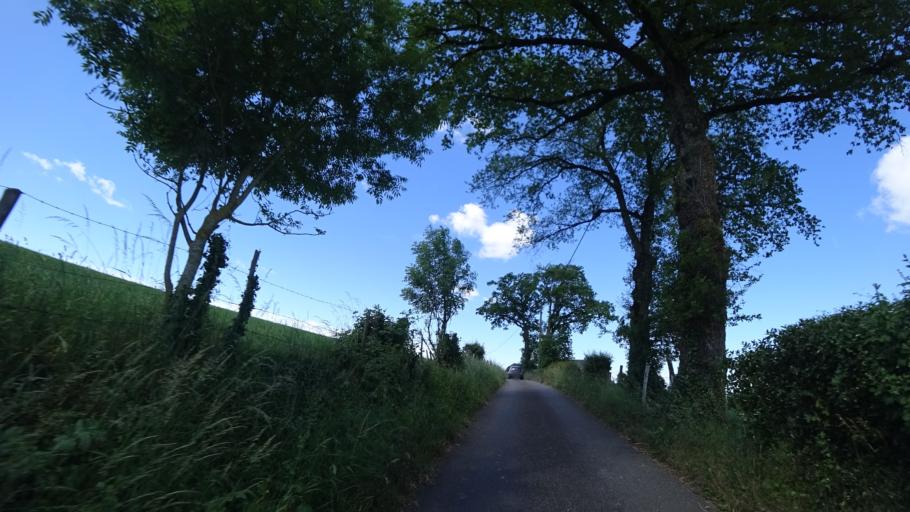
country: FR
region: Midi-Pyrenees
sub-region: Departement de l'Aveyron
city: Colombies
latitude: 44.3941
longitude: 2.3133
